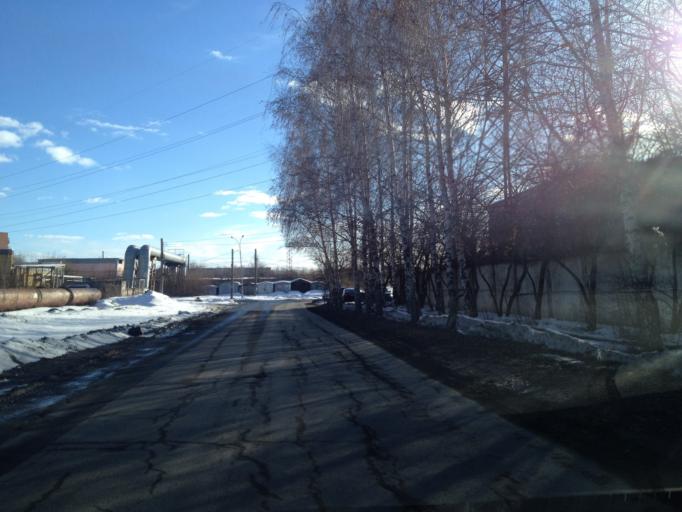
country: RU
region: Sverdlovsk
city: Yekaterinburg
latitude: 56.8749
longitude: 60.5429
